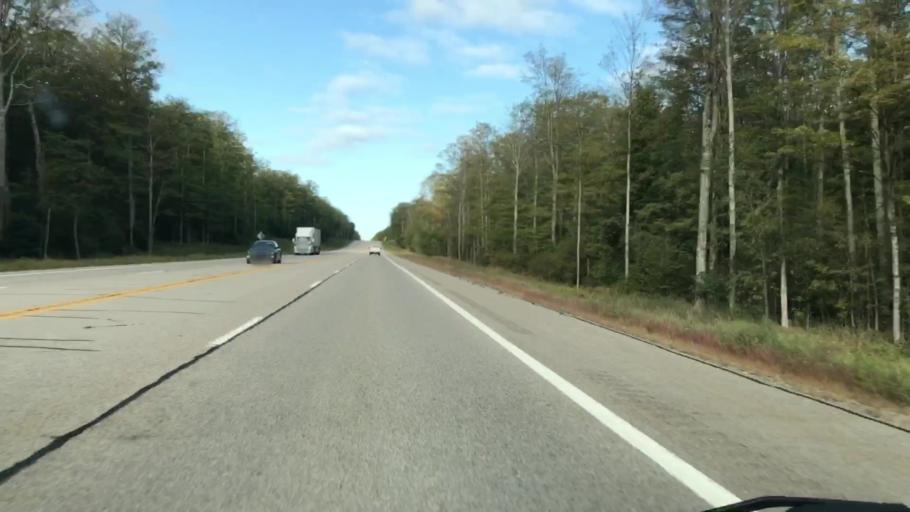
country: US
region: Michigan
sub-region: Luce County
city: Newberry
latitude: 46.3322
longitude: -85.1049
